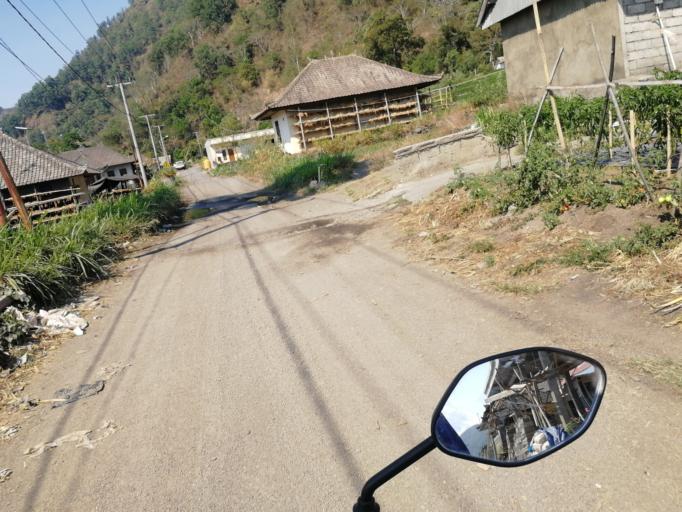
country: ID
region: Bali
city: Banjar Trunyan
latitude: -8.2647
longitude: 115.4205
